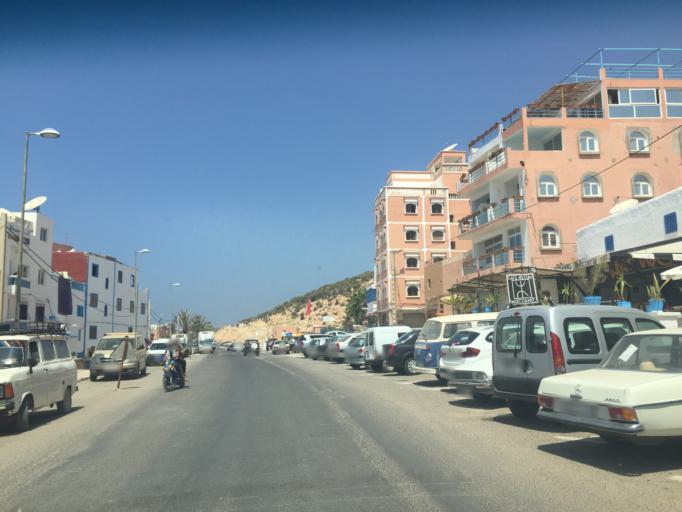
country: MA
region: Souss-Massa-Draa
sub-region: Agadir-Ida-ou-Tnan
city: Taghazout
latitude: 30.5452
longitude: -9.7088
